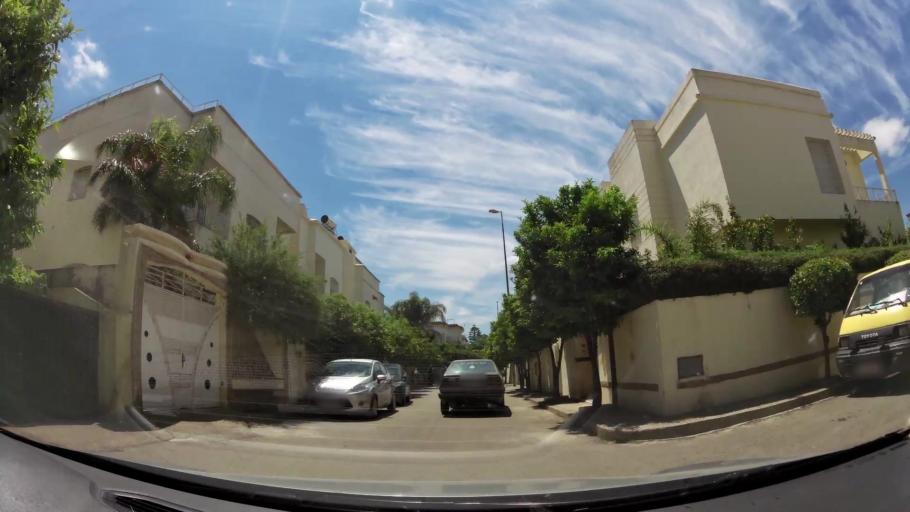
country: MA
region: Fes-Boulemane
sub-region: Fes
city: Fes
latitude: 34.0132
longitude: -4.9915
